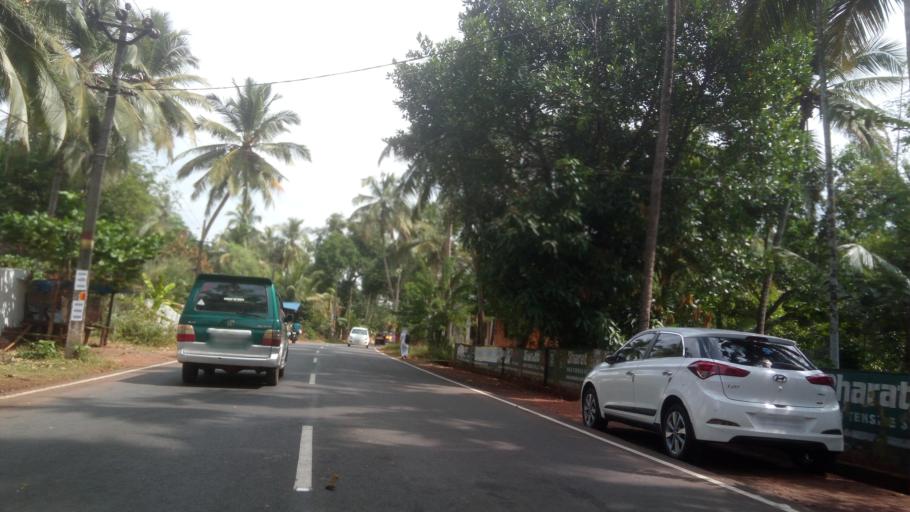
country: IN
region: Kerala
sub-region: Malappuram
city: Tirur
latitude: 10.8676
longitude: 75.9995
